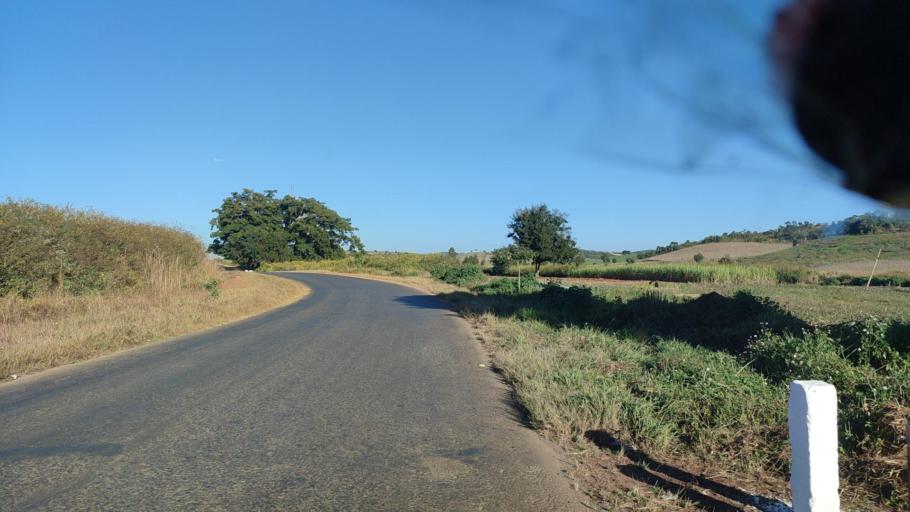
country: MM
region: Mandalay
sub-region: Pyin Oo Lwin District
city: Pyin Oo Lwin
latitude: 22.3937
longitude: 96.9331
